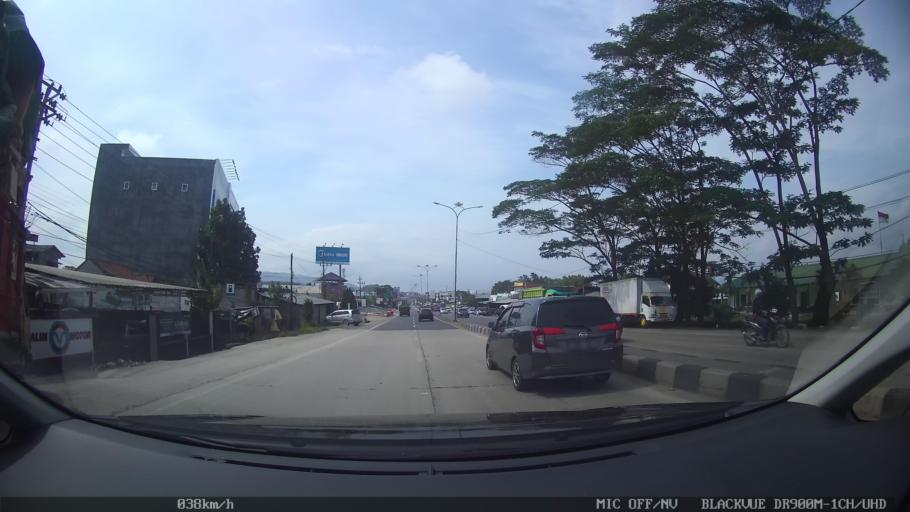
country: ID
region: Lampung
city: Kedaton
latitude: -5.3862
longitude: 105.2871
